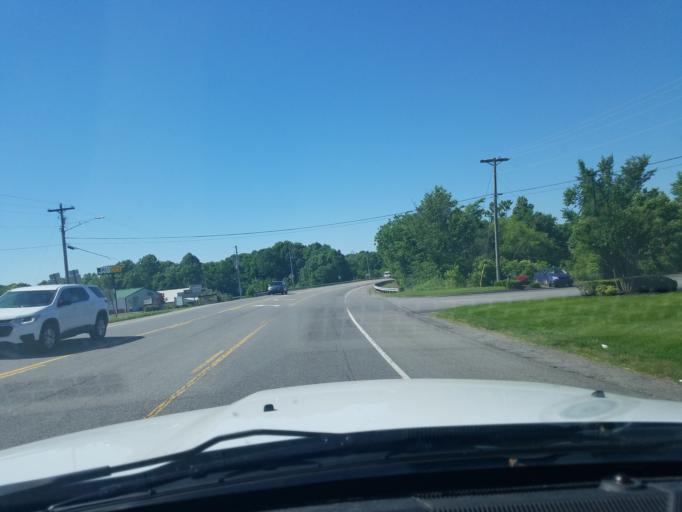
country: US
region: Tennessee
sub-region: Sumner County
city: Westmoreland
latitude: 36.5519
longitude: -86.2365
